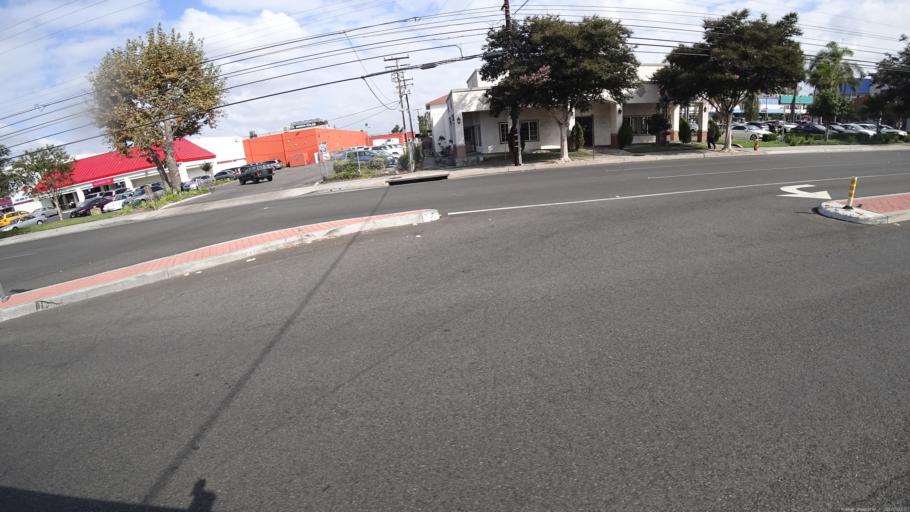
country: US
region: California
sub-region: Orange County
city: Garden Grove
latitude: 33.7595
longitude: -117.9528
